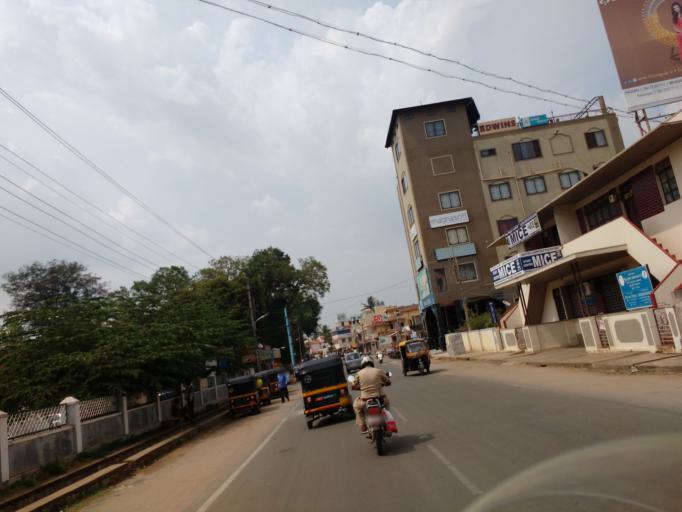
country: IN
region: Karnataka
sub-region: Hassan
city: Hassan
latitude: 13.0106
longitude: 76.1030
